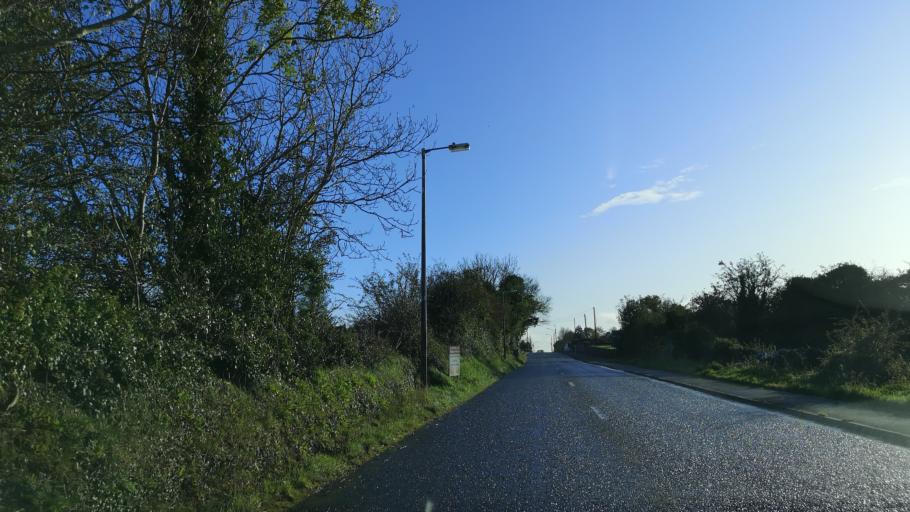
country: IE
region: Connaught
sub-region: Roscommon
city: Castlerea
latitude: 53.7778
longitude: -8.4885
